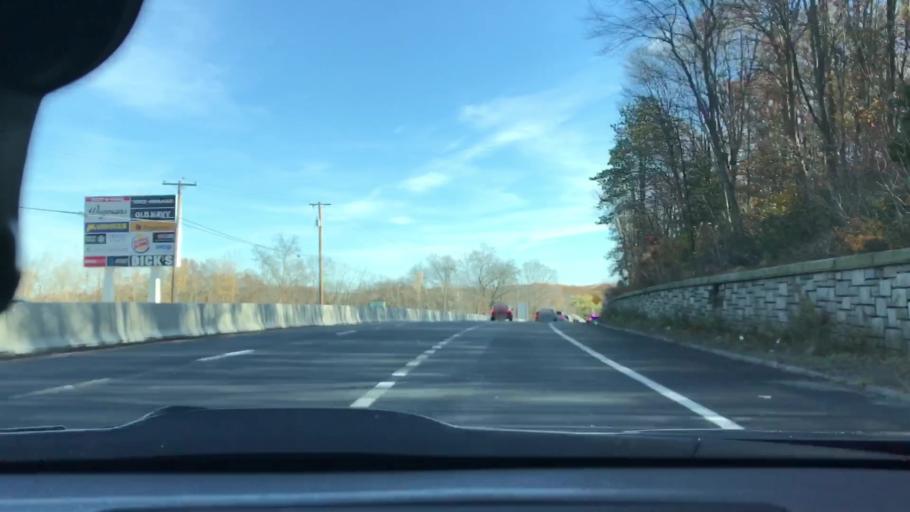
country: US
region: Massachusetts
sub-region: Worcester County
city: Northborough
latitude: 42.2833
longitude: -71.6674
